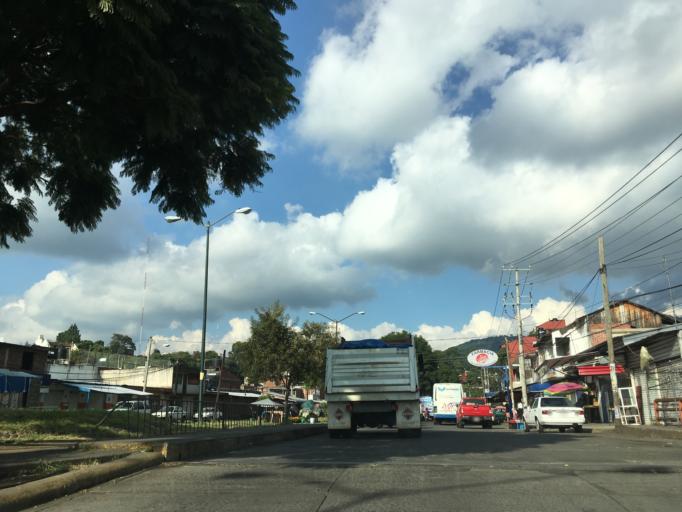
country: MX
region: Michoacan
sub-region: Uruapan
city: Uruapan
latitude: 19.4319
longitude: -102.0757
